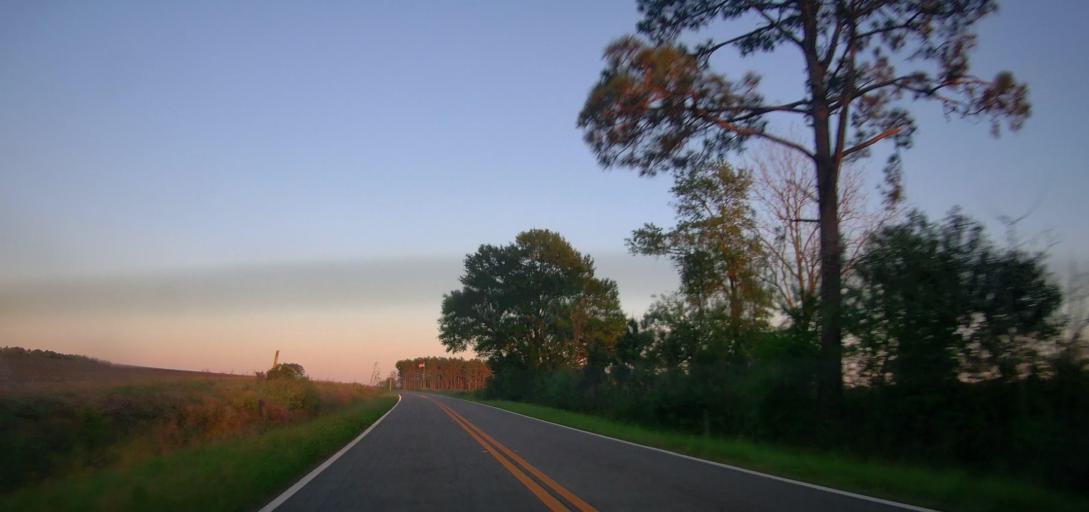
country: US
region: Georgia
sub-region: Ben Hill County
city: Fitzgerald
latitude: 31.7703
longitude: -83.3789
